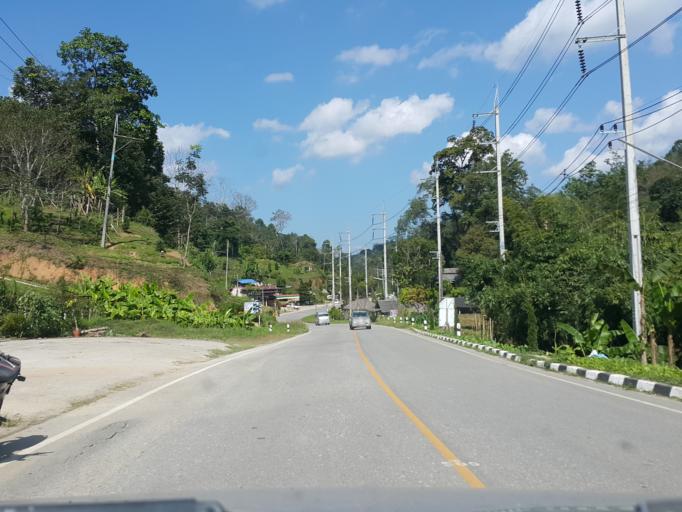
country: TH
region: Chiang Mai
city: Mae Taeng
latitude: 19.1633
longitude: 98.6903
